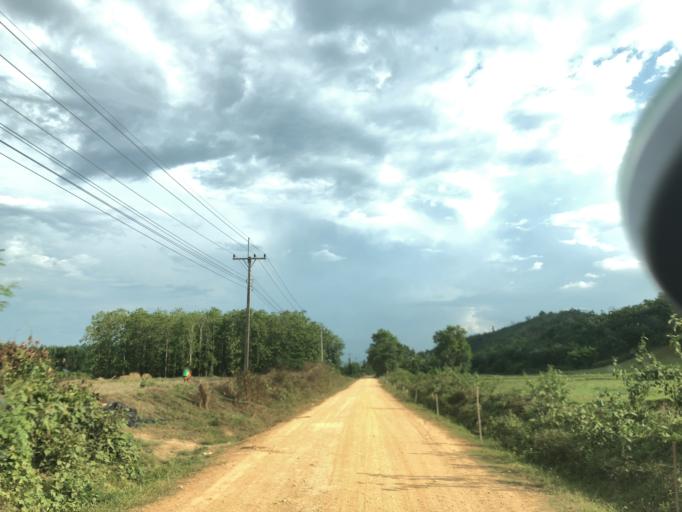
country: TH
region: Loei
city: Chiang Khan
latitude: 18.0038
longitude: 101.4203
